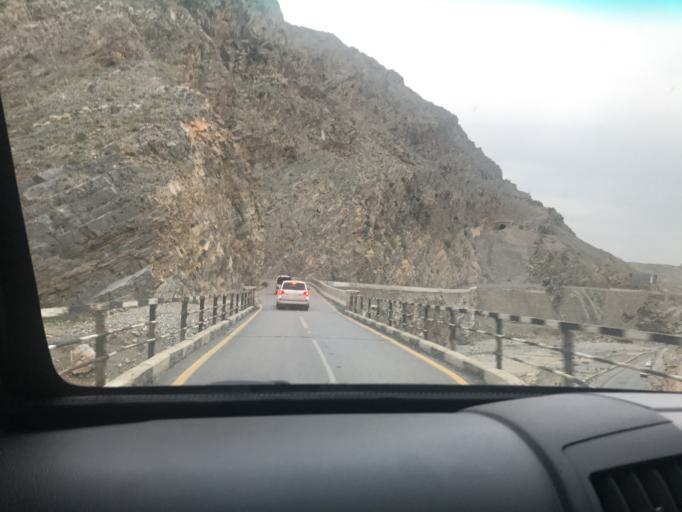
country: PK
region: Federally Administered Tribal Areas
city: Landi Kotal
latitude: 34.0356
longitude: 71.2577
